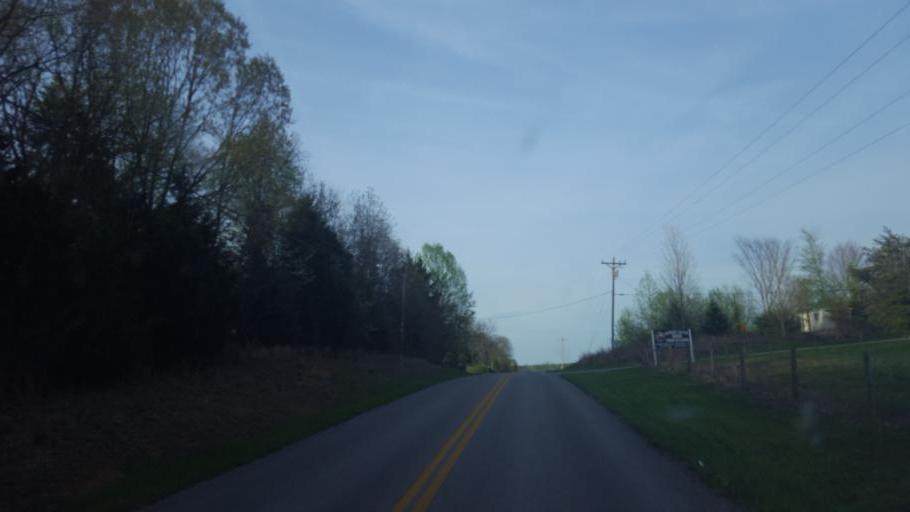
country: US
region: Kentucky
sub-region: Barren County
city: Glasgow
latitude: 36.9300
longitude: -86.0912
